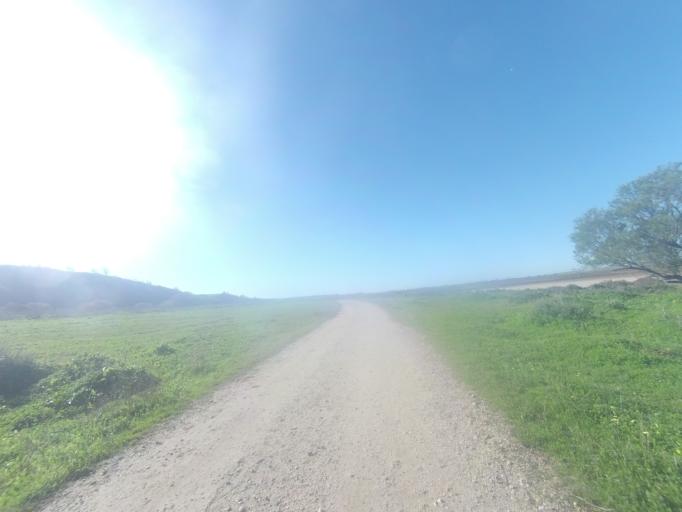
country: ES
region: Andalusia
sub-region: Provincia de Huelva
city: Palos de la Frontera
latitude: 37.2427
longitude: -6.8885
